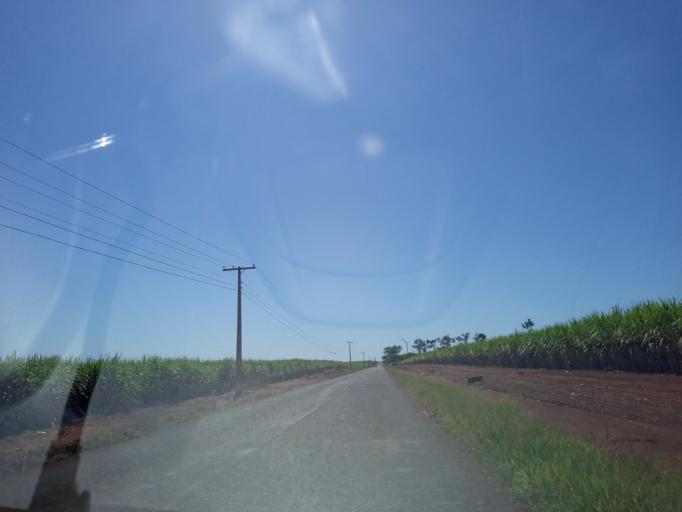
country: BR
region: Goias
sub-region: Itumbiara
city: Itumbiara
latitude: -18.4262
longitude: -49.1777
